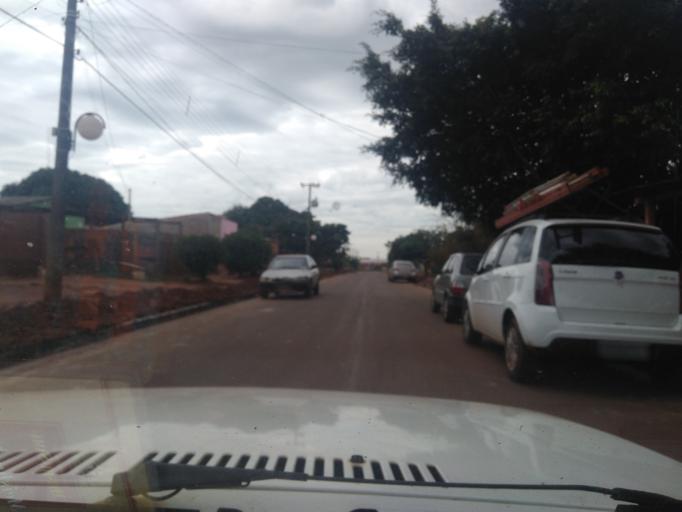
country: BR
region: Mato Grosso do Sul
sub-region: Ponta Pora
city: Ponta Pora
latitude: -22.5088
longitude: -55.7339
